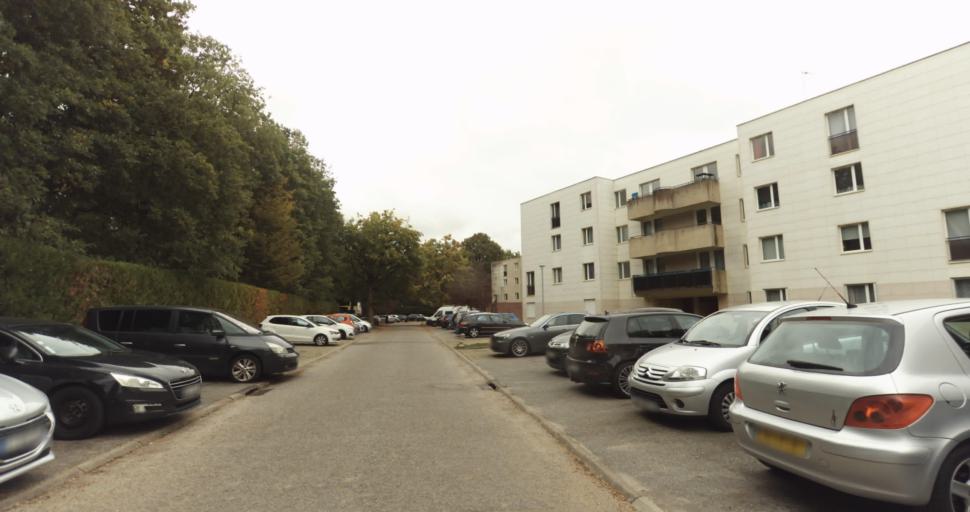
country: FR
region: Centre
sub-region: Departement d'Eure-et-Loir
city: Vernouillet
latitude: 48.7107
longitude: 1.3563
